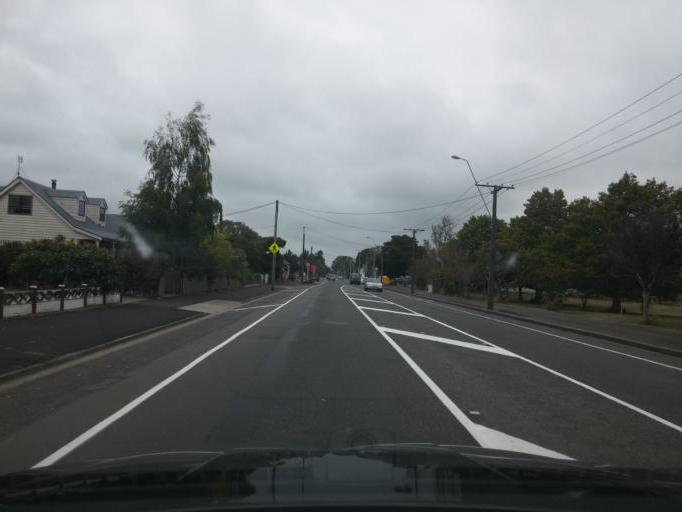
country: NZ
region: Wellington
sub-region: Masterton District
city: Masterton
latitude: -41.0891
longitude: 175.4508
